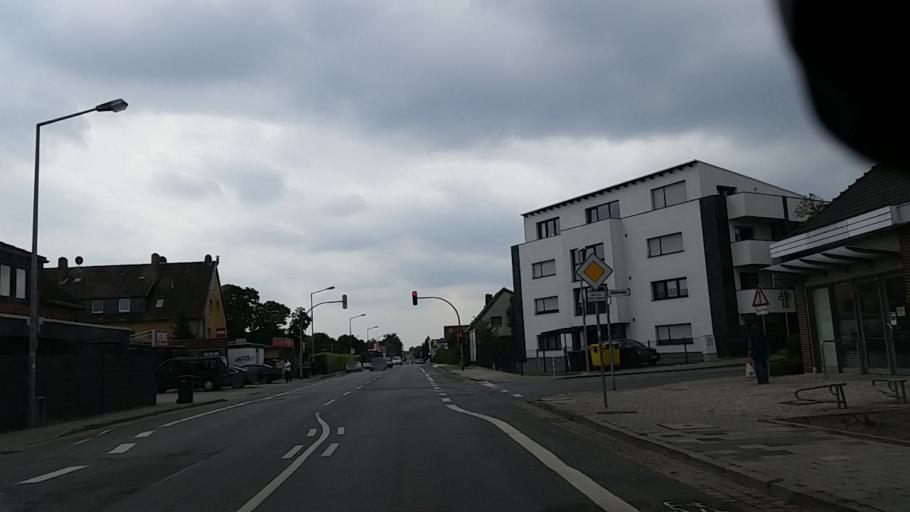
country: DE
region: Lower Saxony
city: Ruhen
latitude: 52.4483
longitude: 10.8469
